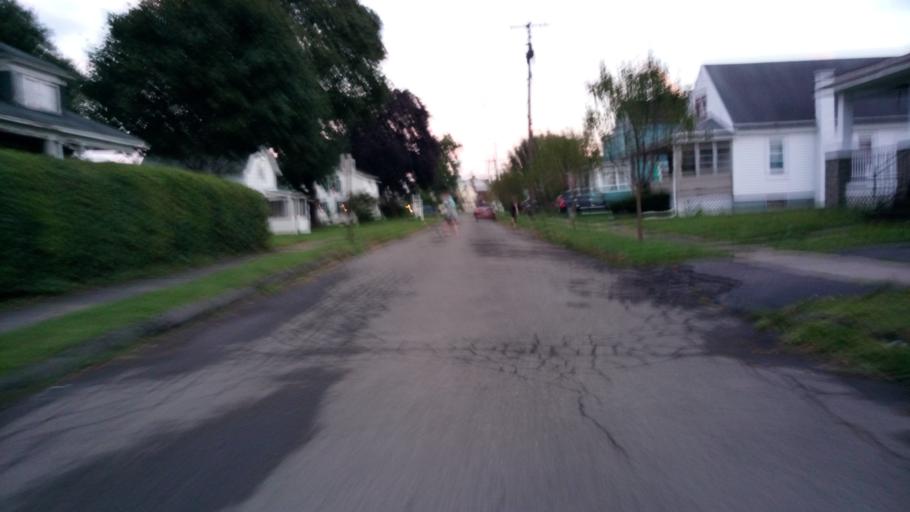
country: US
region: New York
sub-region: Chemung County
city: Elmira
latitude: 42.1044
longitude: -76.8241
